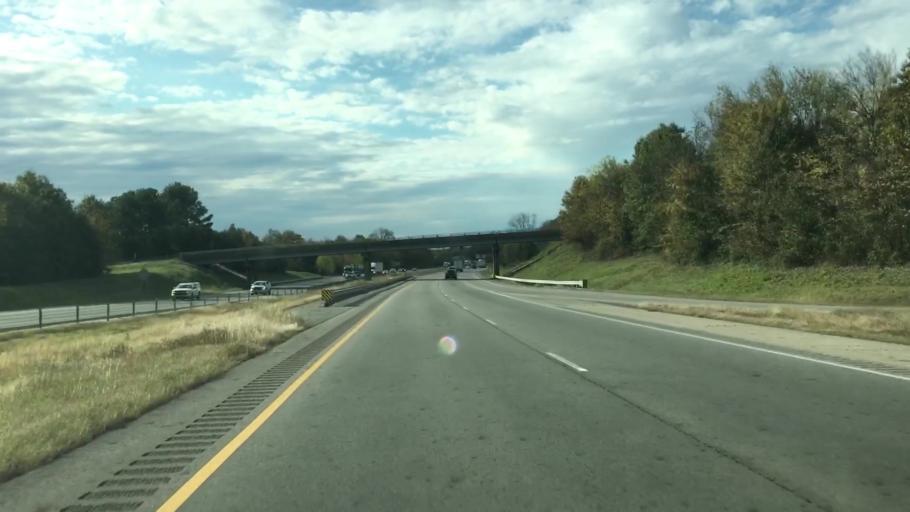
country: US
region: Arkansas
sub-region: Pope County
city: Pottsville
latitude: 35.2494
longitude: -93.0336
